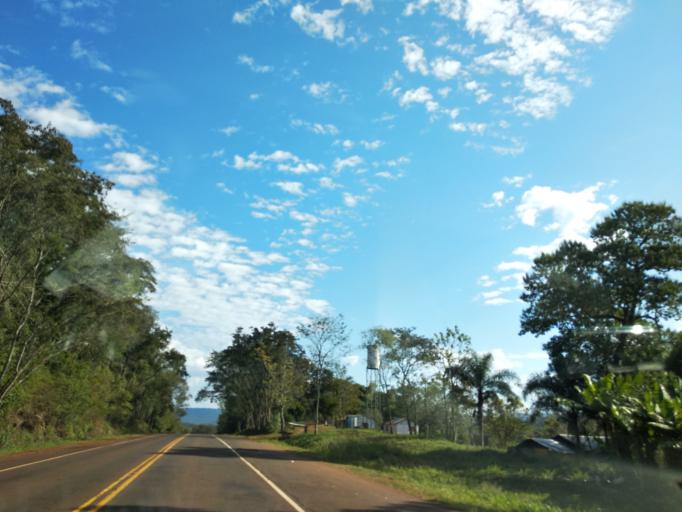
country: AR
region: Misiones
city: Aristobulo del Valle
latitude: -27.0972
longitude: -54.9569
